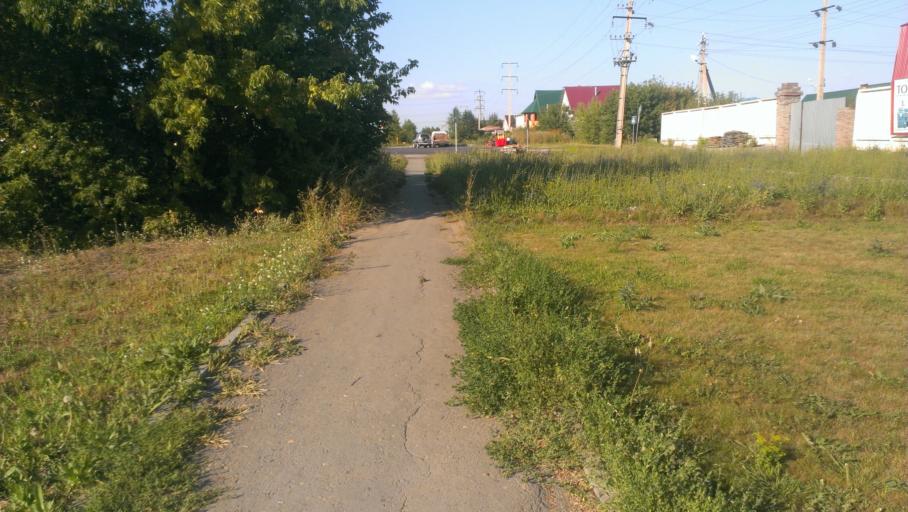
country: RU
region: Altai Krai
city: Novosilikatnyy
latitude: 53.3562
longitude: 83.6366
